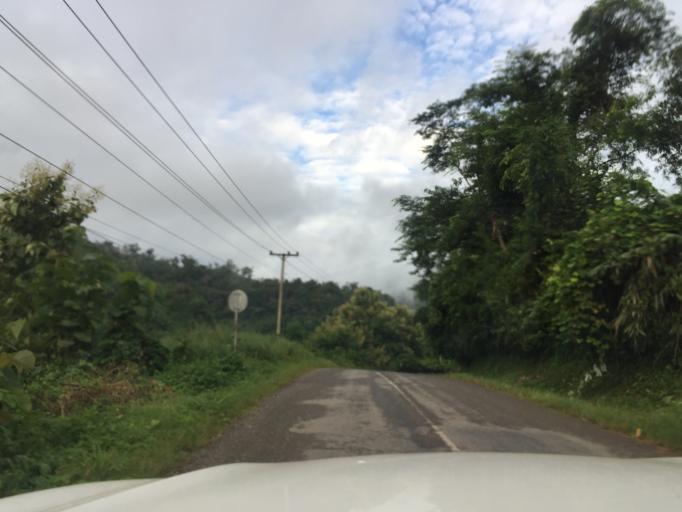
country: LA
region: Phongsali
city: Khoa
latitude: 21.1015
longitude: 102.2633
